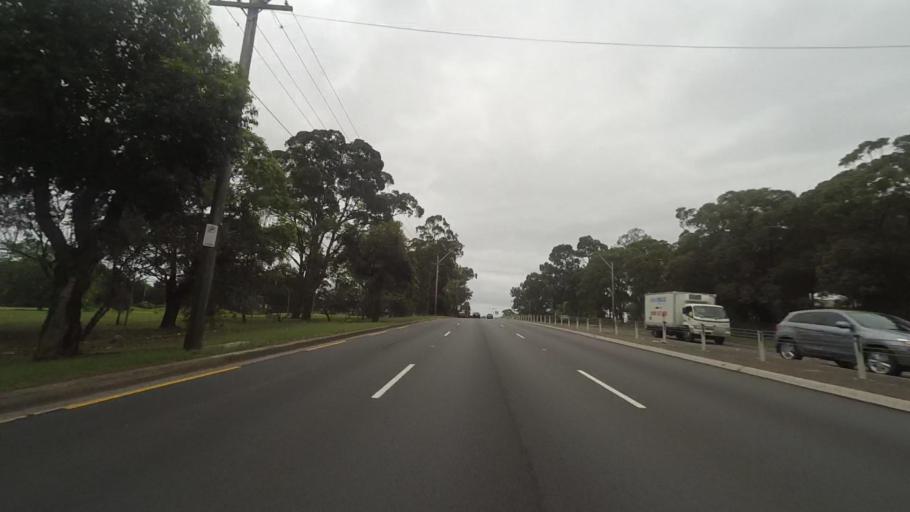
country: AU
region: New South Wales
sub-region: Auburn
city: Berala
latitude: -33.8750
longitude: 151.0416
